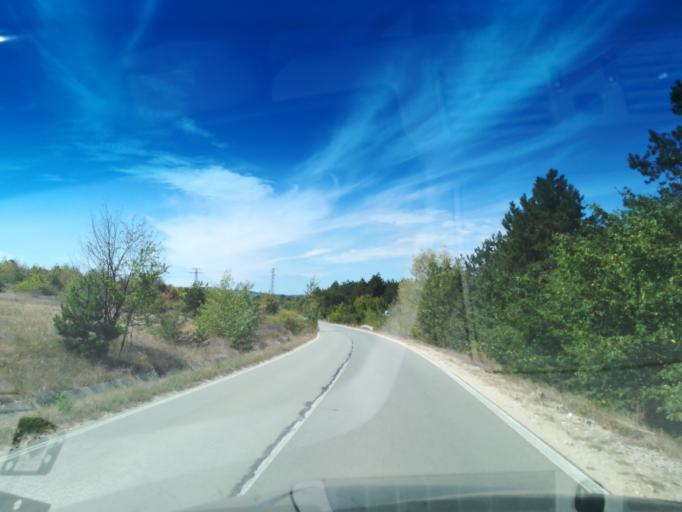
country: BG
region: Plovdiv
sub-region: Obshtina Suedinenie
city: Suedinenie
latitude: 42.3975
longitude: 24.5576
